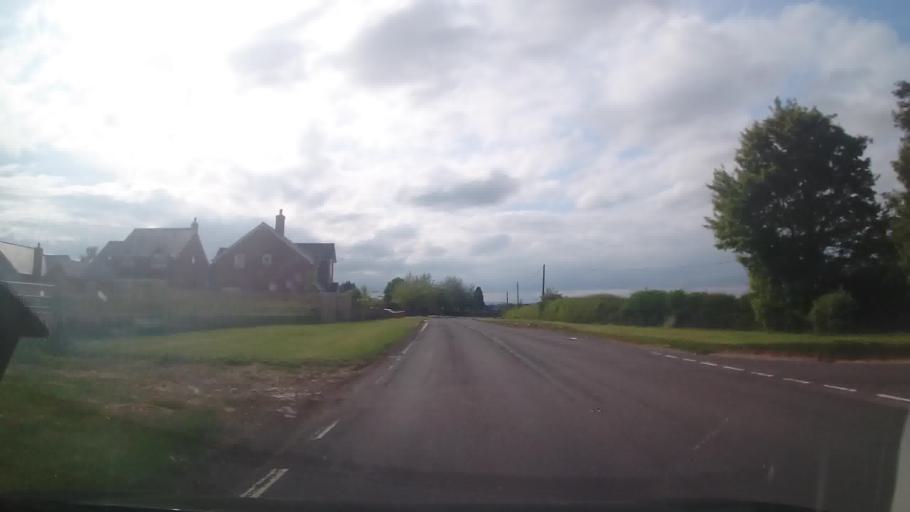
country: GB
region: England
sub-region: Shropshire
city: Petton
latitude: 52.8092
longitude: -2.7821
